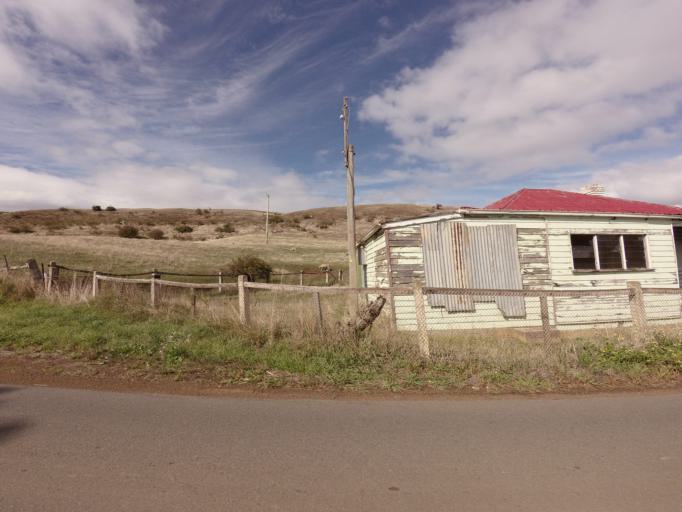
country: AU
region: Tasmania
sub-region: Derwent Valley
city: New Norfolk
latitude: -42.7075
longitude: 146.9129
